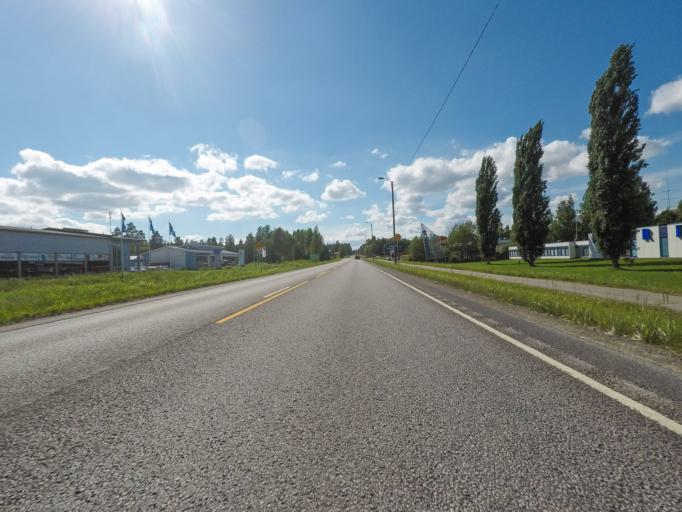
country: FI
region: Southern Savonia
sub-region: Savonlinna
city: Savonlinna
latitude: 61.8774
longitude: 28.9802
